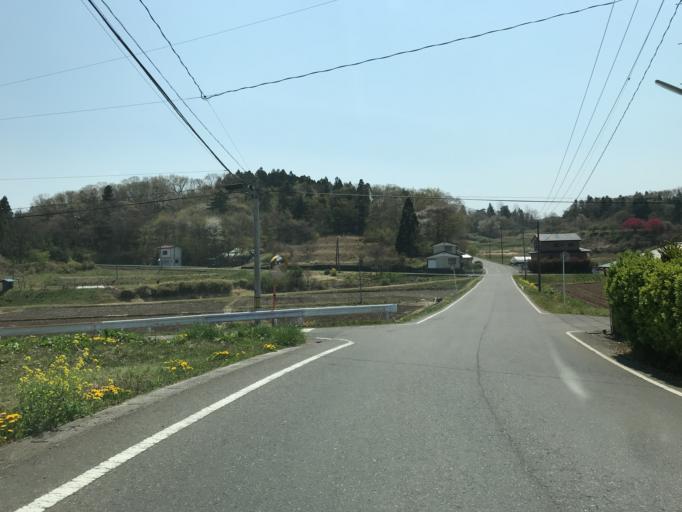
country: JP
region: Fukushima
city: Ishikawa
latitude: 37.1065
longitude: 140.4010
